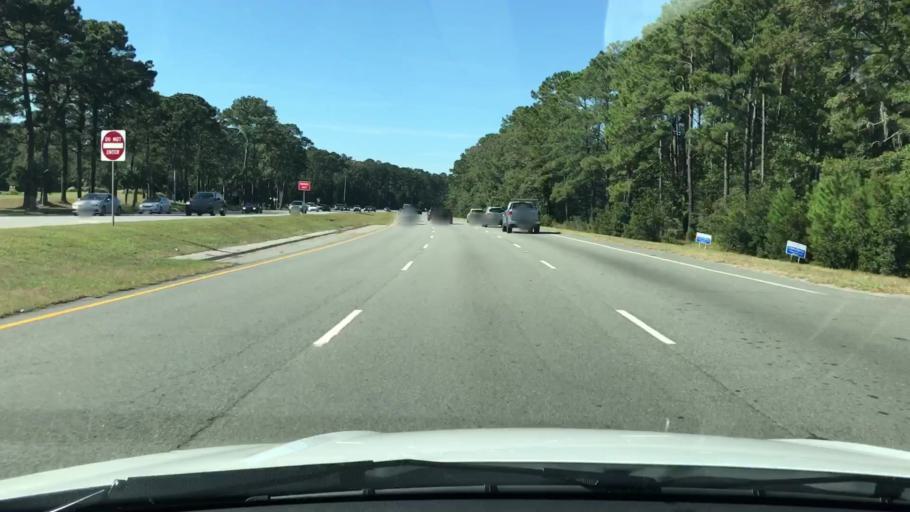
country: US
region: South Carolina
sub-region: Beaufort County
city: Bluffton
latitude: 32.2862
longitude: -80.8878
